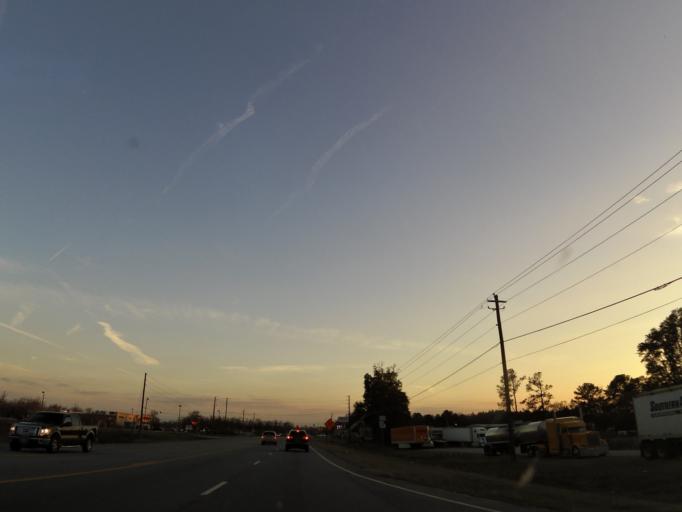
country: US
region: Georgia
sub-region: Lee County
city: Leesburg
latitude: 31.6594
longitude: -84.1729
